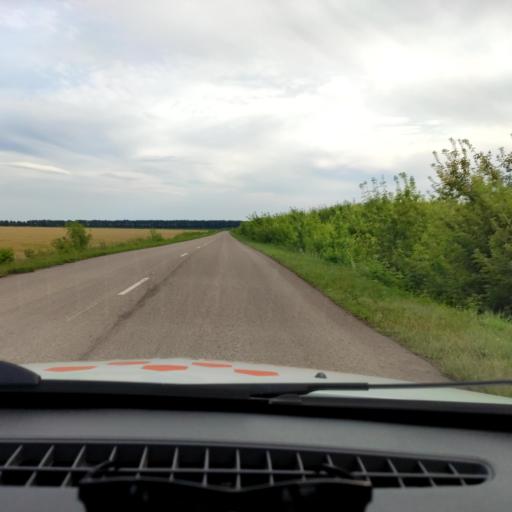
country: RU
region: Bashkortostan
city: Avdon
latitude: 54.5322
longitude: 55.6414
